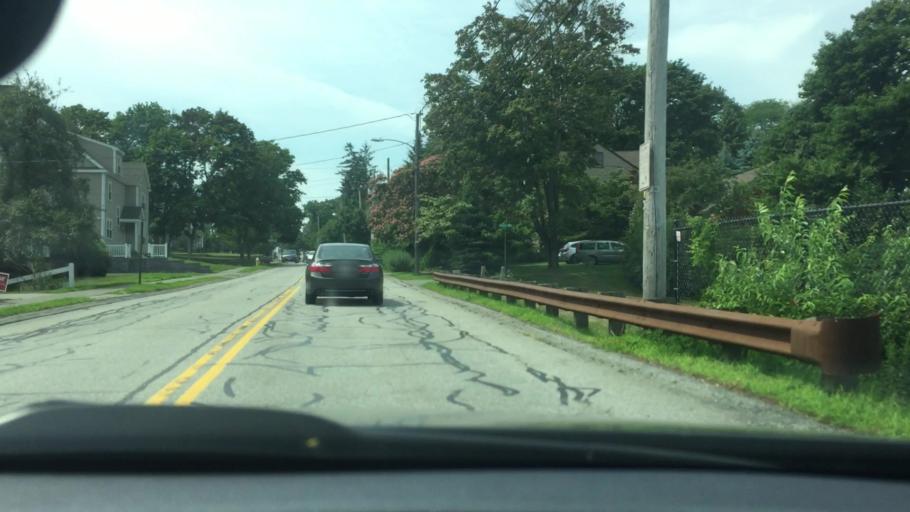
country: US
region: Massachusetts
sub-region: Norfolk County
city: Needham
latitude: 42.2994
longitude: -71.2352
